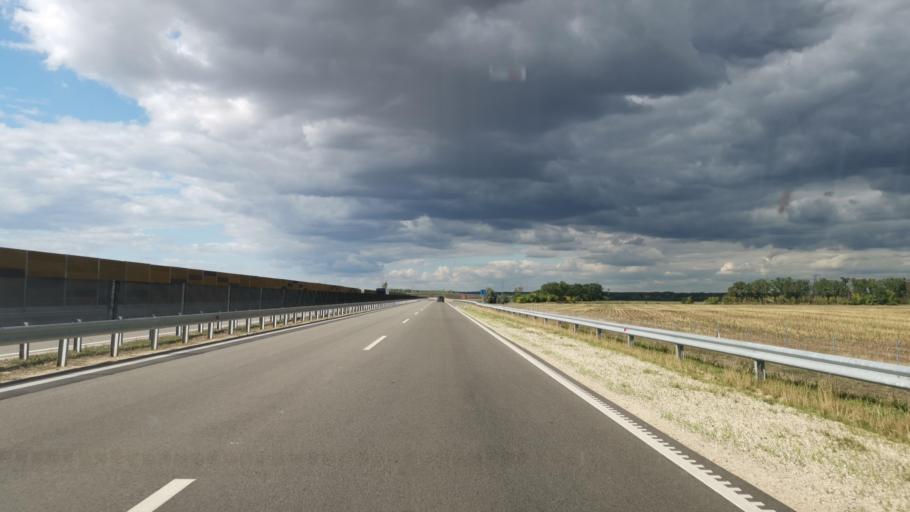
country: HU
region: Jasz-Nagykun-Szolnok
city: Tiszapuspoki
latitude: 47.1960
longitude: 20.3327
